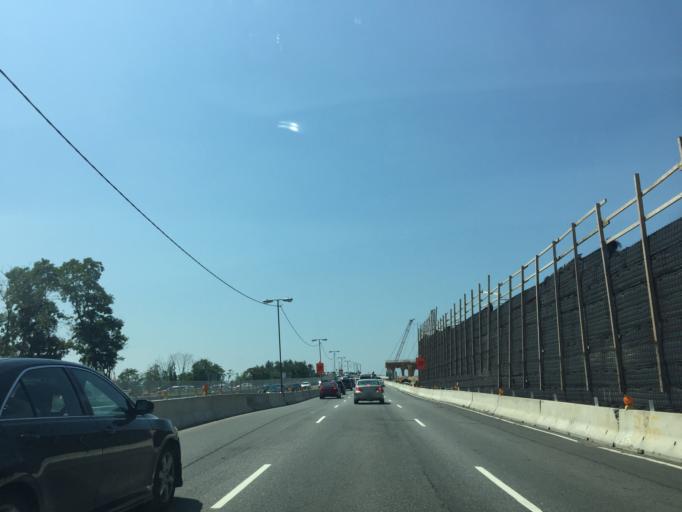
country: US
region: New York
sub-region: Kings County
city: East New York
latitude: 40.6089
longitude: -73.8976
